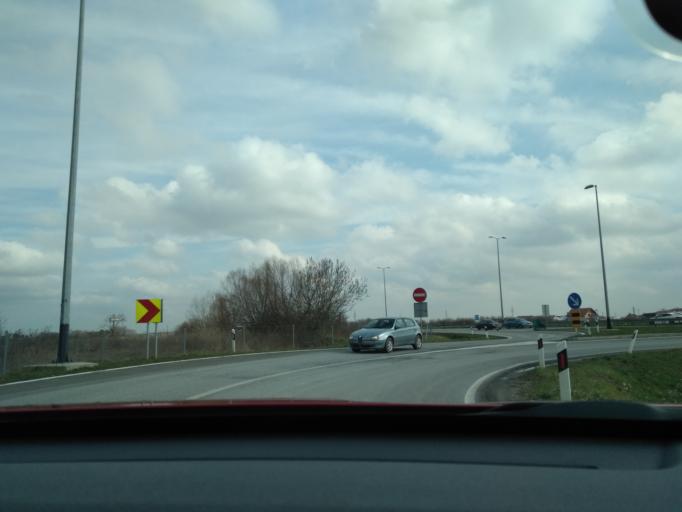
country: HR
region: Osjecko-Baranjska
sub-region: Grad Osijek
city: Osijek
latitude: 45.5429
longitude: 18.6790
